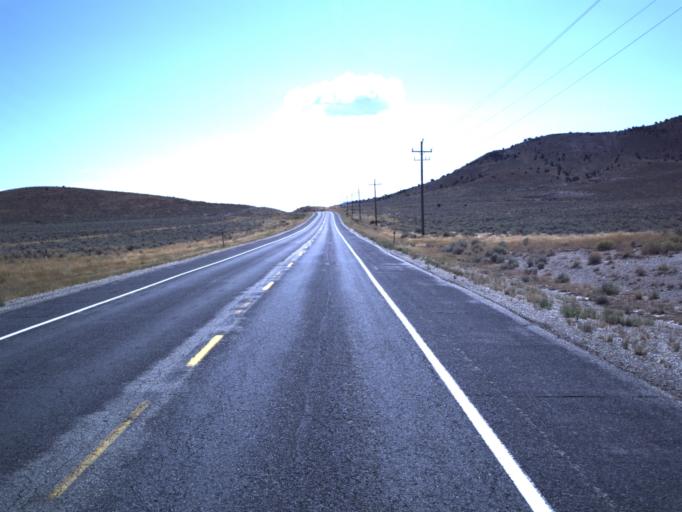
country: US
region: Utah
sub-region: Utah County
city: Eagle Mountain
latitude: 40.0743
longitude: -112.3814
